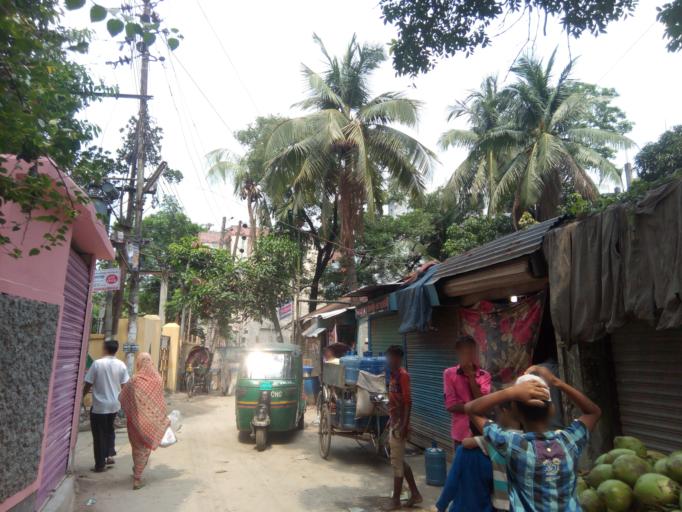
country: BD
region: Dhaka
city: Paltan
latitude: 23.7339
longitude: 90.4327
